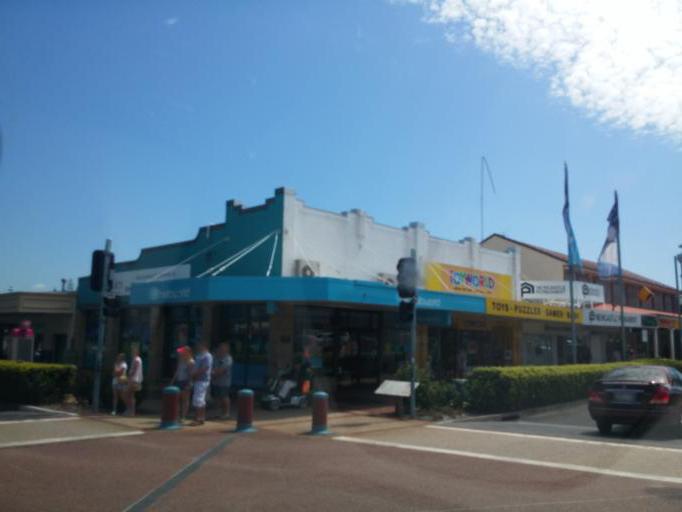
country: AU
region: New South Wales
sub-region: Port Macquarie-Hastings
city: Port Macquarie
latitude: -31.4313
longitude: 152.9083
